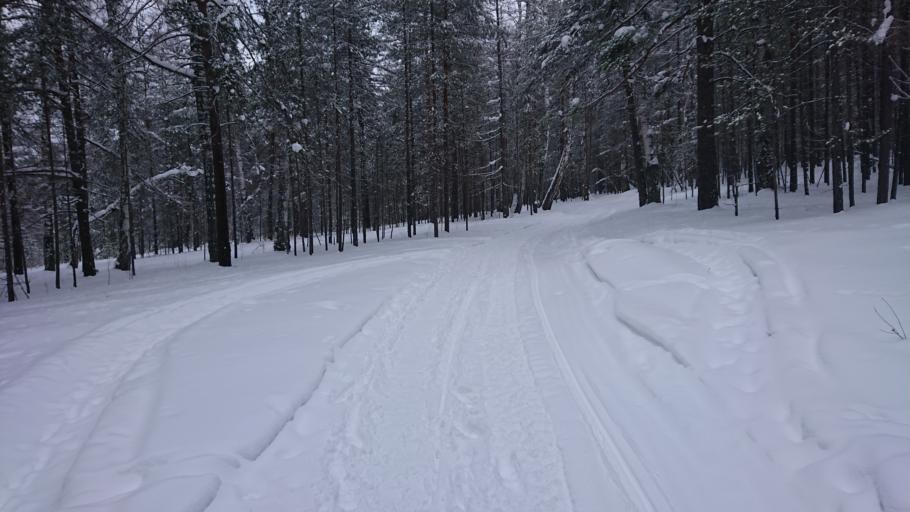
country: RU
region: Sverdlovsk
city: Degtyarsk
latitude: 56.6920
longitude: 60.0656
